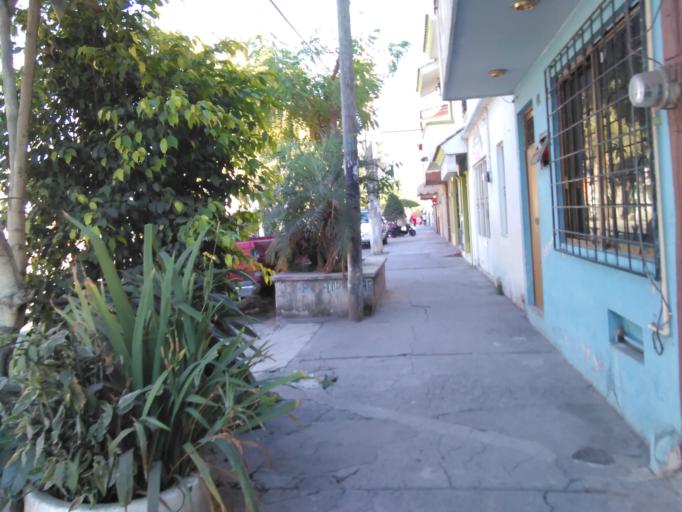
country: MX
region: Nayarit
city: Tepic
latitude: 21.5238
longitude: -104.8876
